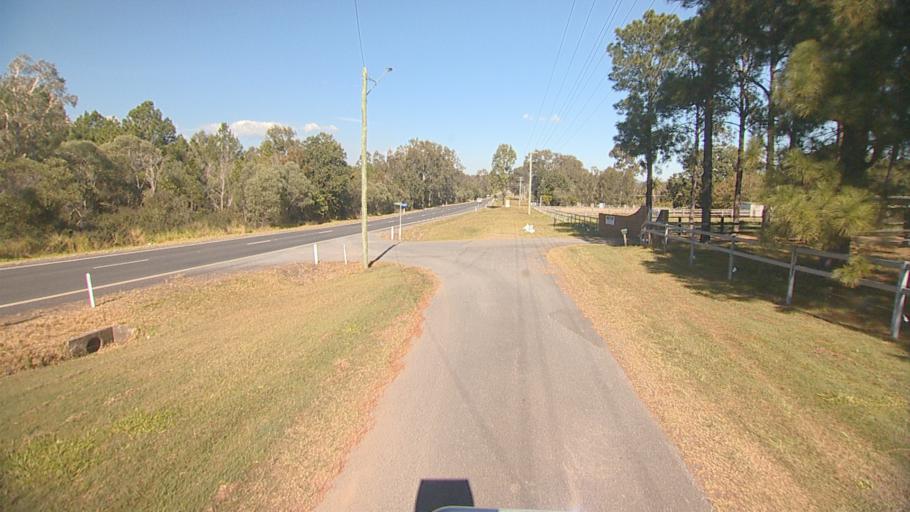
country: AU
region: Queensland
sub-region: Logan
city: Logan Reserve
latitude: -27.7441
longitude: 153.1264
